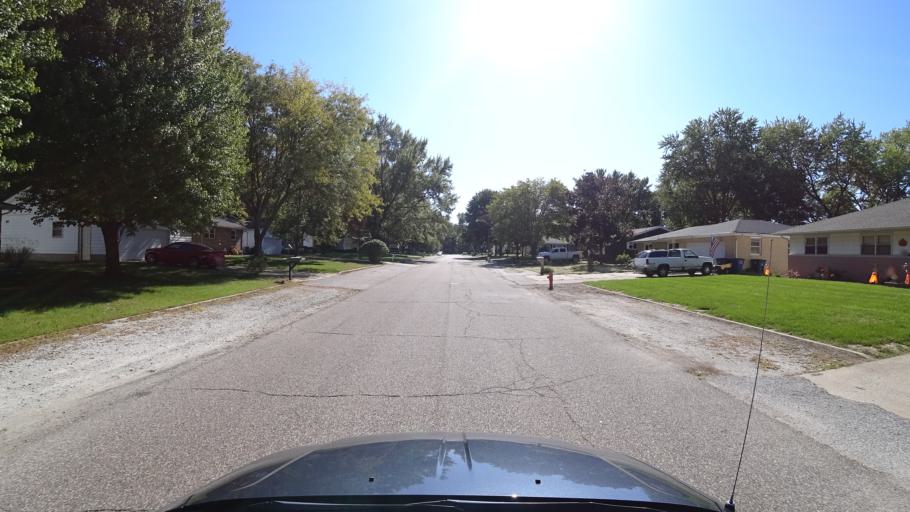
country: US
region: Indiana
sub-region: LaPorte County
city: Michigan City
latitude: 41.6933
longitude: -86.8829
